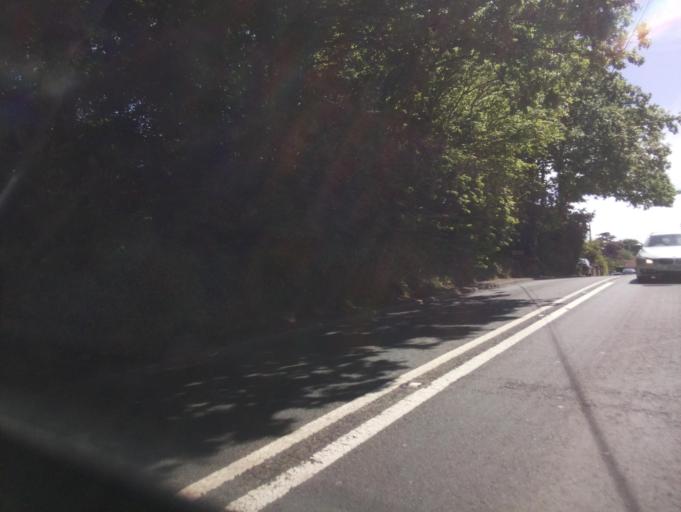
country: GB
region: England
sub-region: Devon
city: Topsham
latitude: 50.6754
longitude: -3.4418
